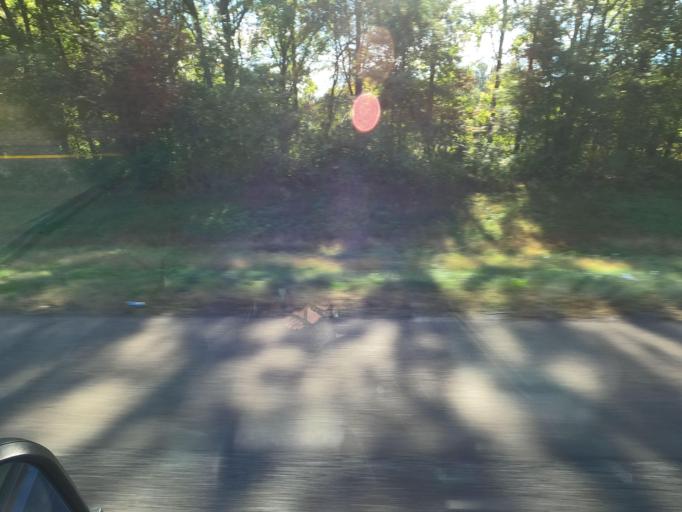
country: US
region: Tennessee
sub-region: Haywood County
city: Brownsville
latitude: 35.4627
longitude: -89.2986
